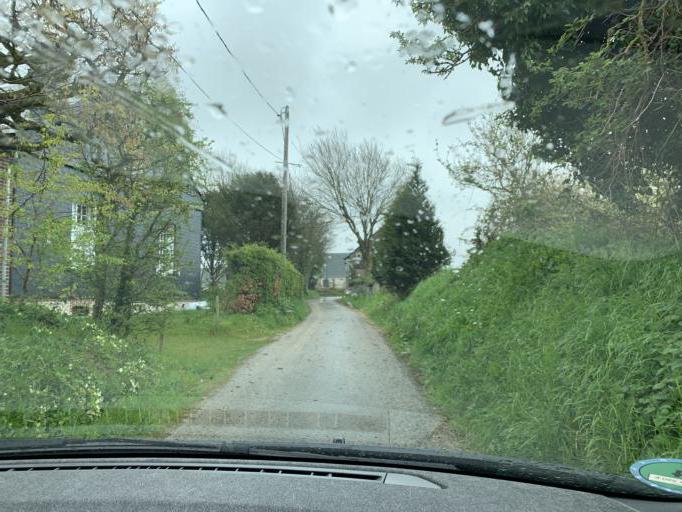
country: FR
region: Haute-Normandie
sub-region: Departement de la Seine-Maritime
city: Les Loges
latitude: 49.7291
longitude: 0.2793
